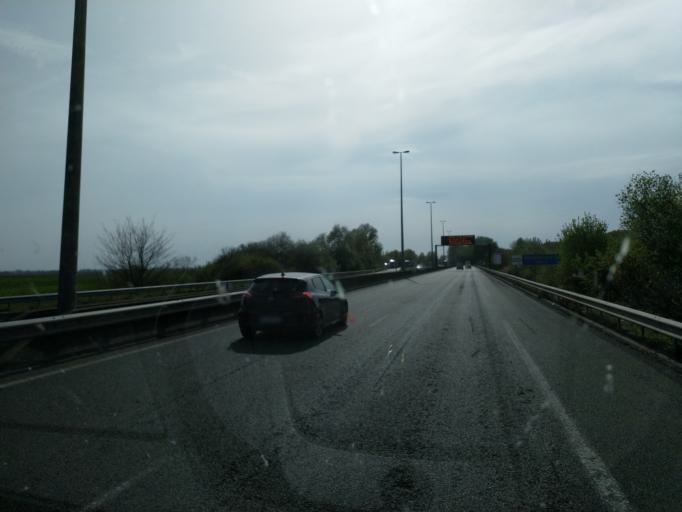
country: FR
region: Nord-Pas-de-Calais
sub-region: Departement du Nord
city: Ghyvelde
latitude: 51.0562
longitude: 2.5614
